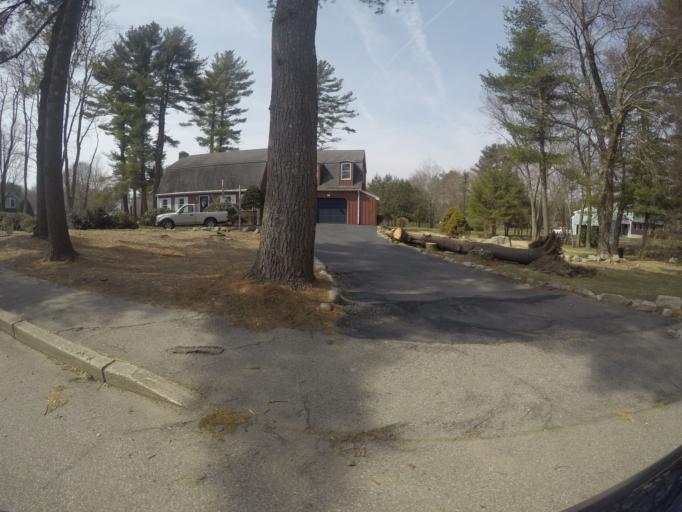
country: US
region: Massachusetts
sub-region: Bristol County
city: Easton
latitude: 42.0464
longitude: -71.1230
